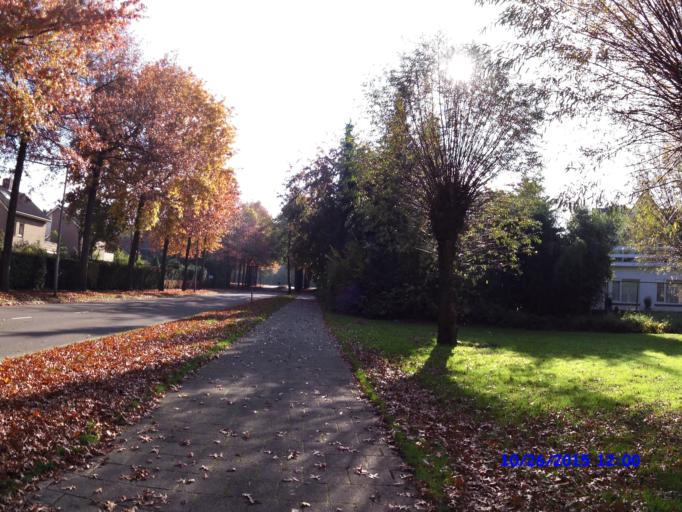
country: NL
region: North Brabant
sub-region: Gemeente Geldrop-Mierlo
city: Mierlo
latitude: 51.4389
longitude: 5.6084
